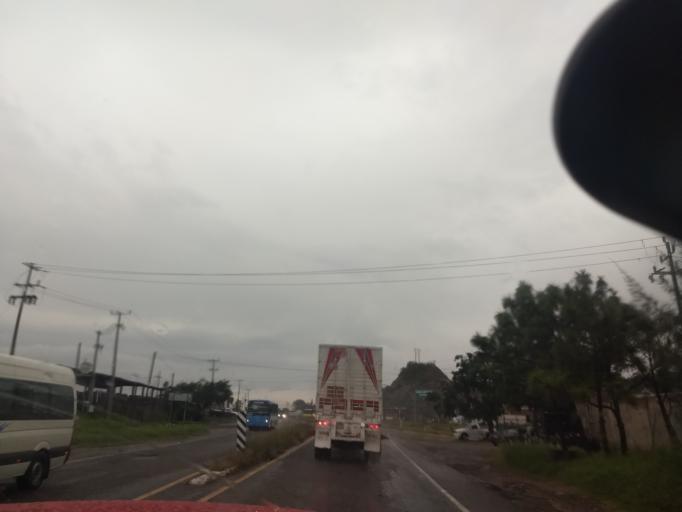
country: MX
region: Jalisco
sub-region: Zapotlan el Grande
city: Ciudad Guzman [CERESO]
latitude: 19.6504
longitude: -103.4732
